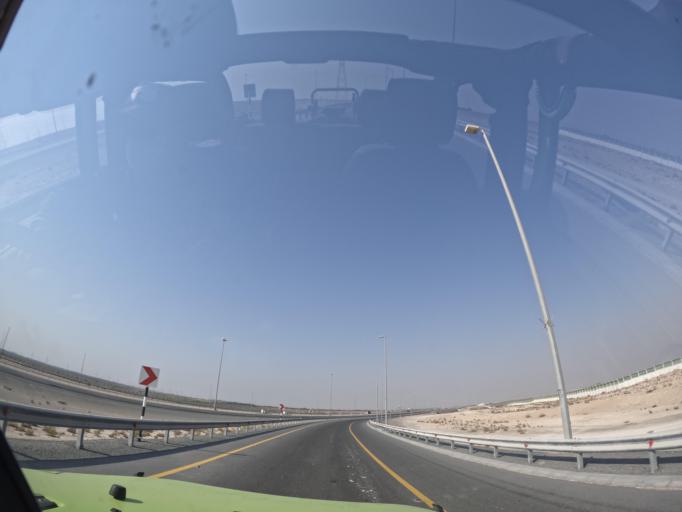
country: AE
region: Abu Dhabi
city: Abu Dhabi
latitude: 24.6173
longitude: 54.7669
